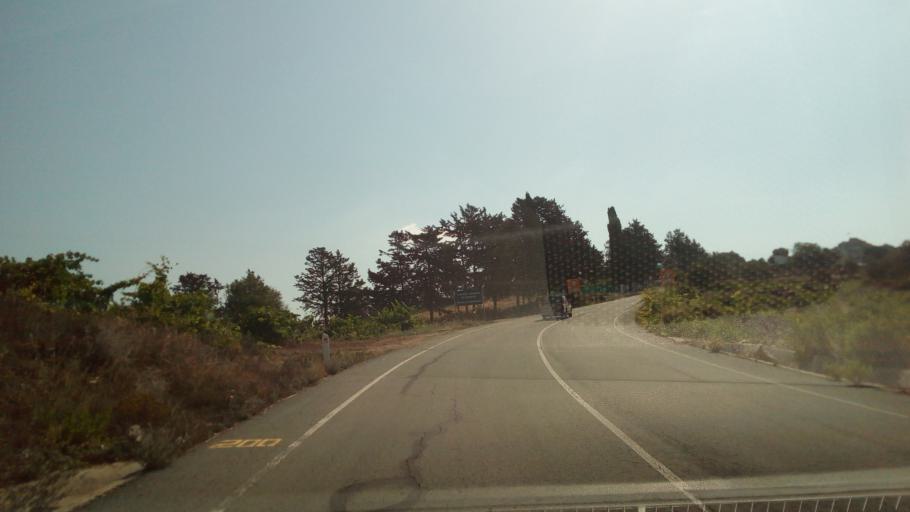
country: CY
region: Limassol
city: Pissouri
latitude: 34.7852
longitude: 32.6132
